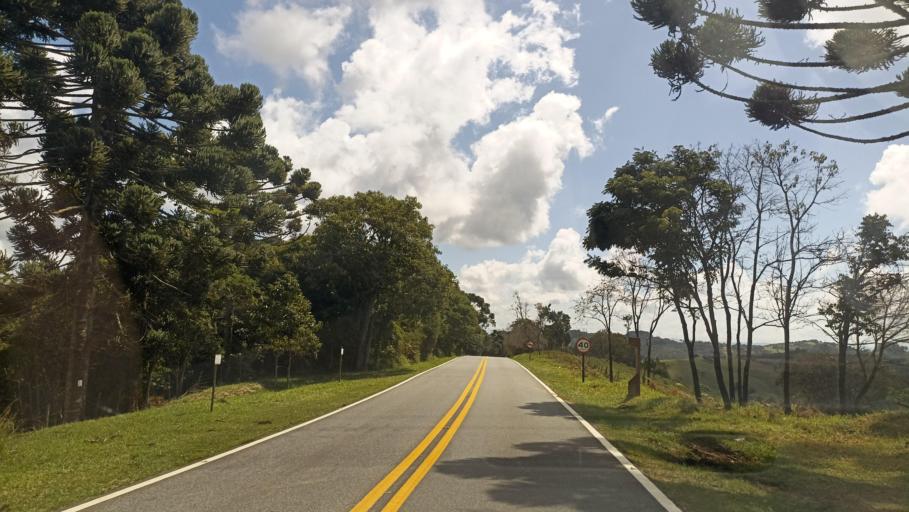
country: BR
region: Sao Paulo
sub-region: Cunha
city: Cunha
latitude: -23.1459
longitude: -44.8895
